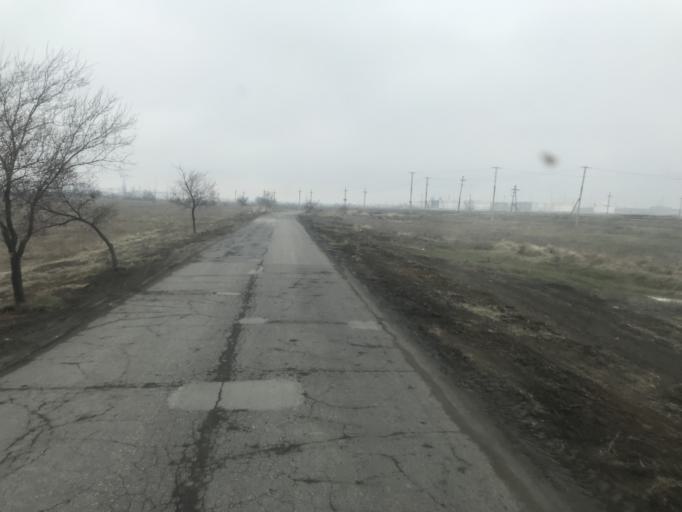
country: RU
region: Volgograd
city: Svetlyy Yar
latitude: 48.4918
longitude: 44.6586
